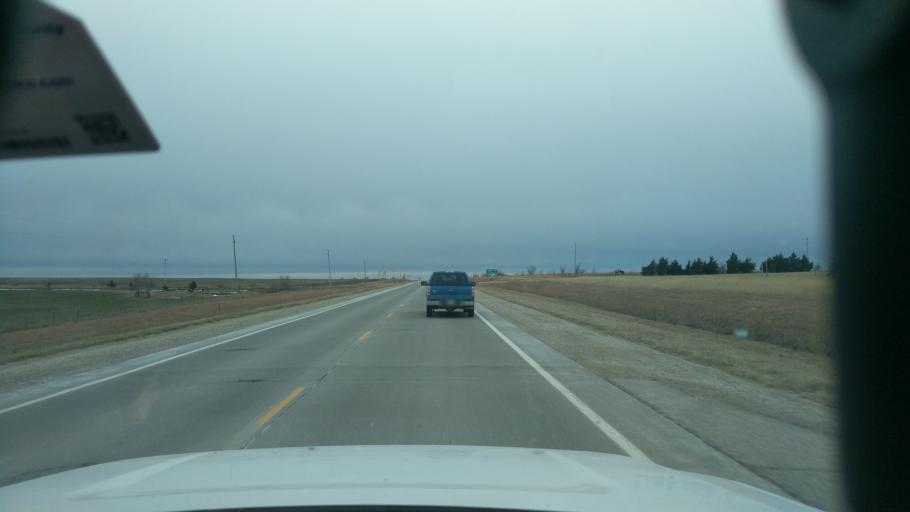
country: US
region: Kansas
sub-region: Dickinson County
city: Herington
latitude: 38.5969
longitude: -96.9483
